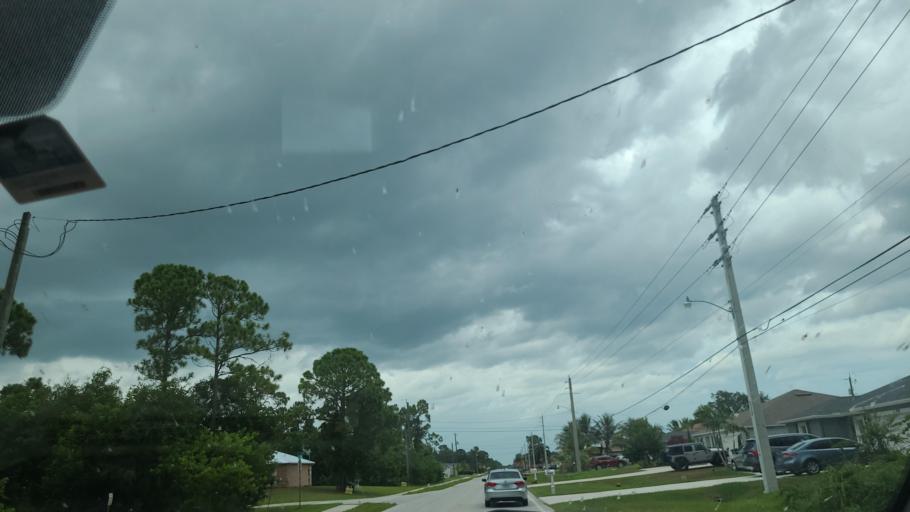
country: US
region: Florida
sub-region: Saint Lucie County
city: Port Saint Lucie
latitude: 27.2450
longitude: -80.3997
